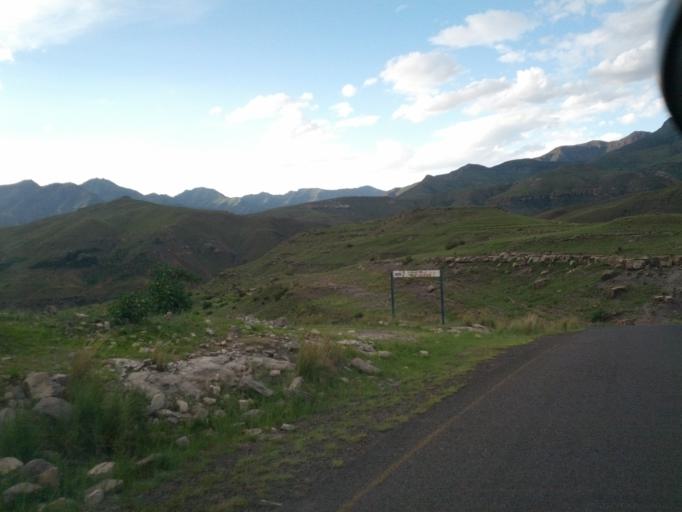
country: LS
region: Qacha's Nek
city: Qacha's Nek
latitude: -30.0709
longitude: 28.5601
